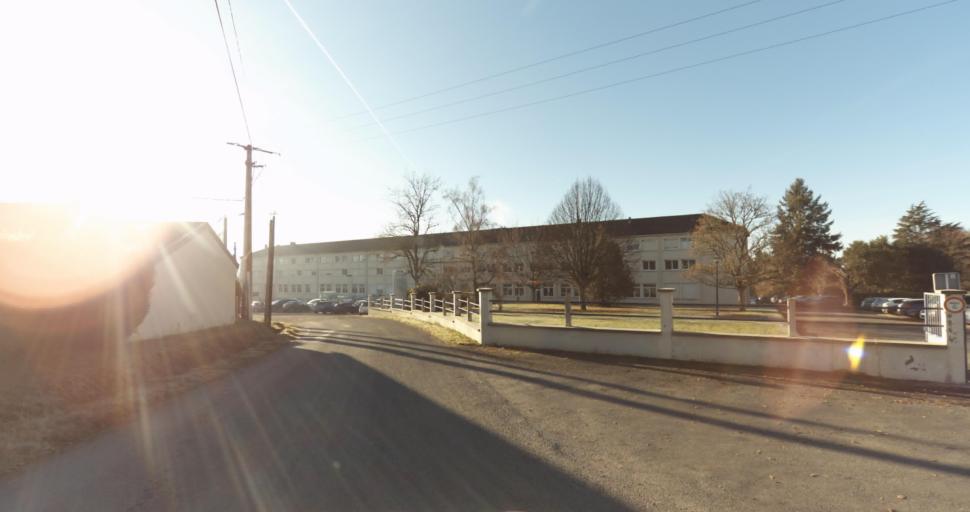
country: FR
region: Limousin
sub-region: Departement de la Haute-Vienne
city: Aixe-sur-Vienne
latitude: 45.8121
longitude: 1.1370
